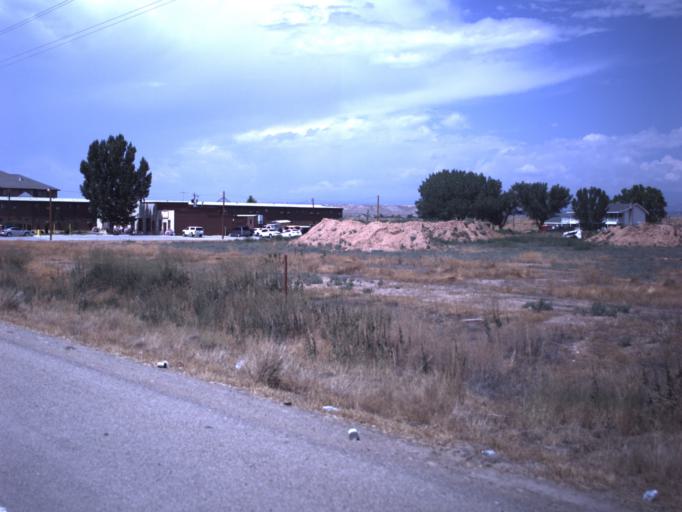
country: US
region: Utah
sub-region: Duchesne County
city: Roosevelt
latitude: 40.3023
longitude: -109.9573
